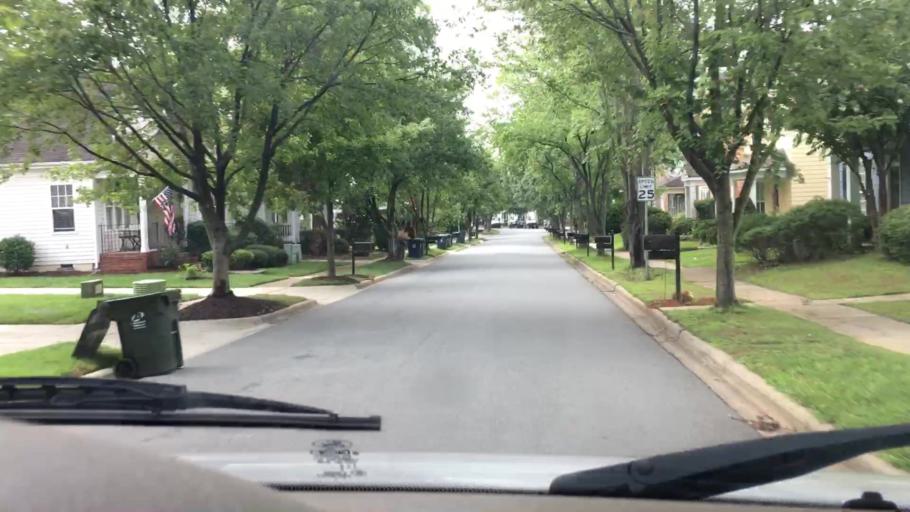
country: US
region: North Carolina
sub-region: Mecklenburg County
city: Cornelius
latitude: 35.4477
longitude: -80.8840
